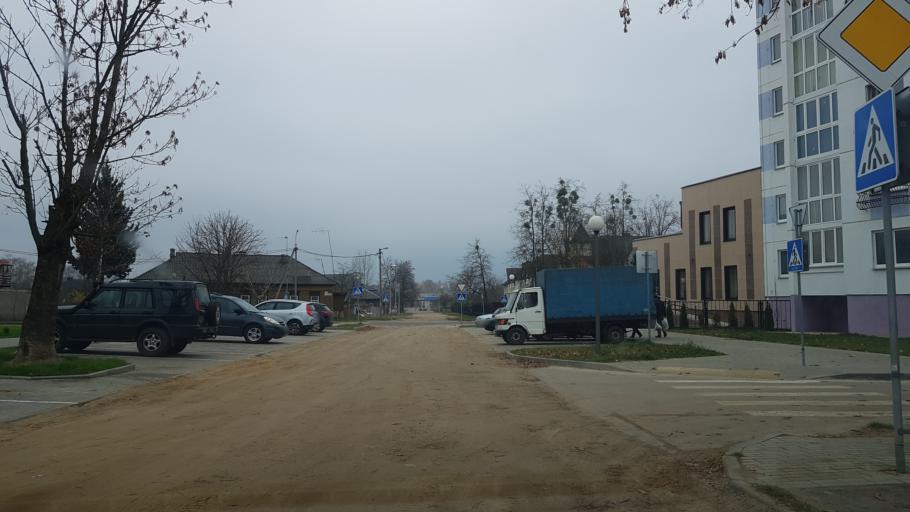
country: BY
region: Mogilev
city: Babruysk
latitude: 53.1531
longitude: 29.2446
